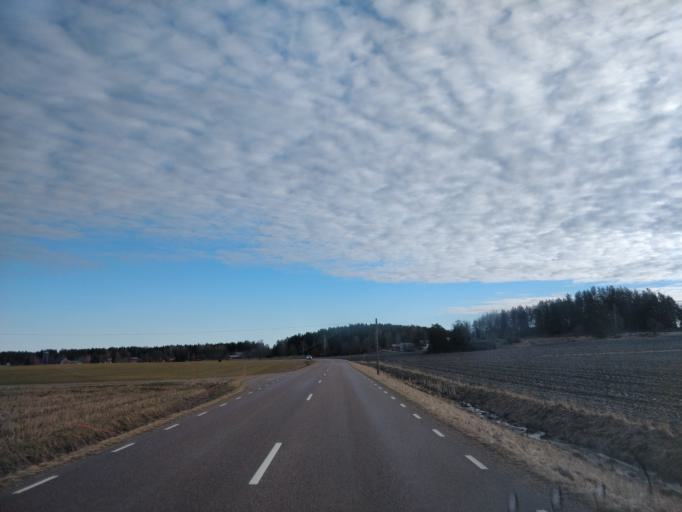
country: SE
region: Uppsala
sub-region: Enkopings Kommun
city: Enkoping
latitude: 59.8051
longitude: 17.0990
